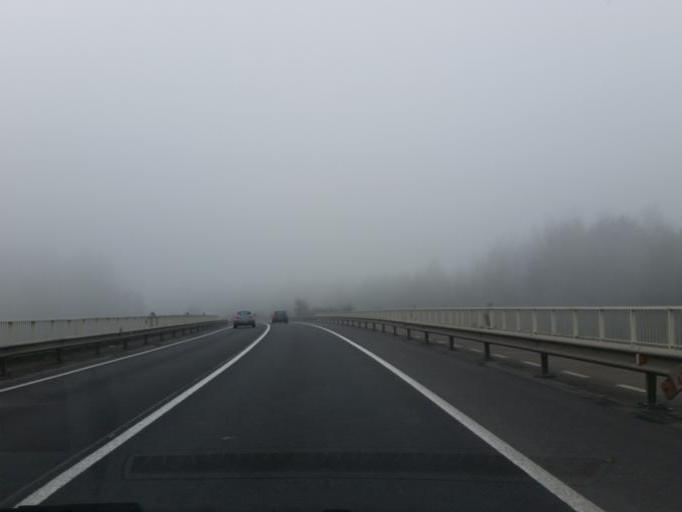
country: BE
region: Flanders
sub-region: Provincie Oost-Vlaanderen
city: Lovendegem
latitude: 51.0830
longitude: 3.6591
